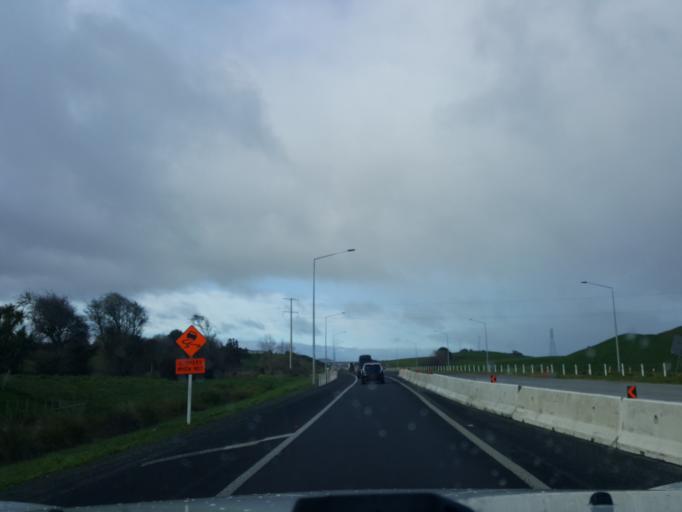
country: NZ
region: Waikato
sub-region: Waikato District
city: Ngaruawahia
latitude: -37.6250
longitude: 175.2061
